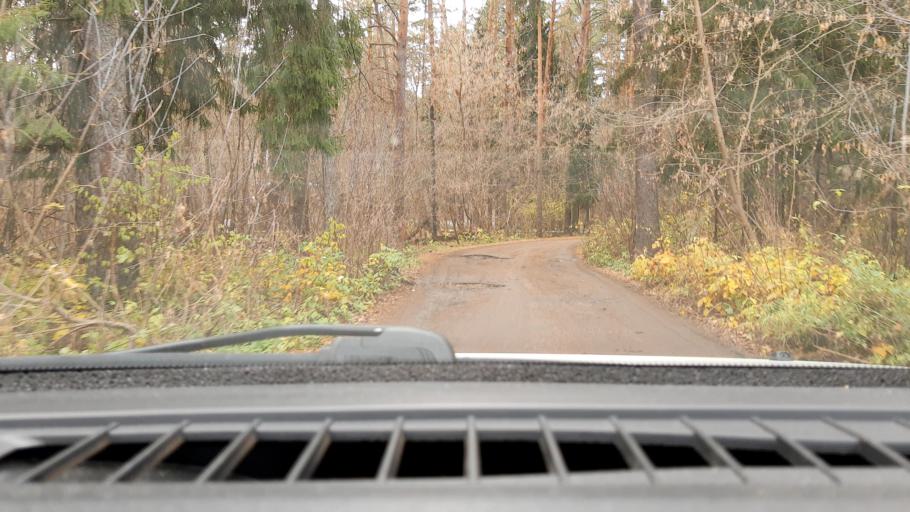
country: RU
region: Nizjnij Novgorod
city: Kstovo
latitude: 56.1690
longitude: 44.1284
